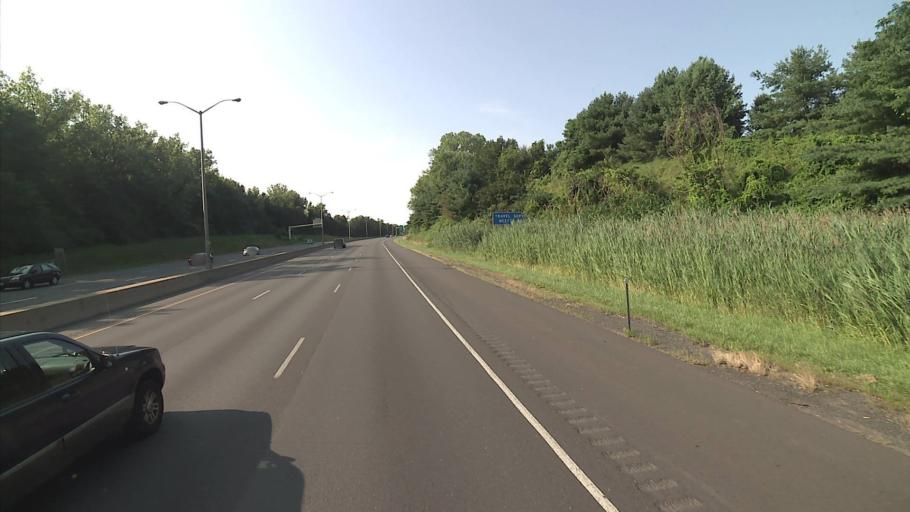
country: US
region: Connecticut
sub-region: Hartford County
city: Thompsonville
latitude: 42.0051
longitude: -72.5853
